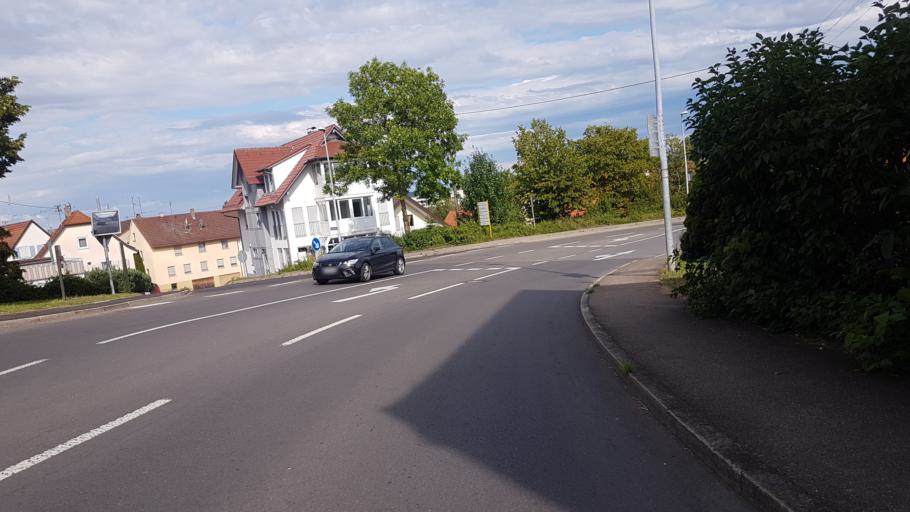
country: DE
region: Baden-Wuerttemberg
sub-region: Tuebingen Region
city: Rottenacker
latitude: 48.2330
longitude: 9.6884
